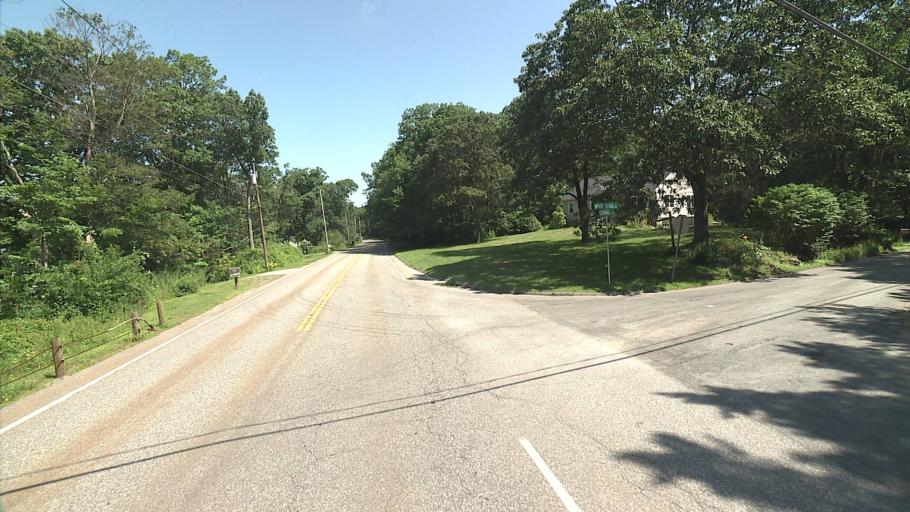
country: US
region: Connecticut
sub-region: Litchfield County
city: New Preston
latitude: 41.7702
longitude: -73.3535
